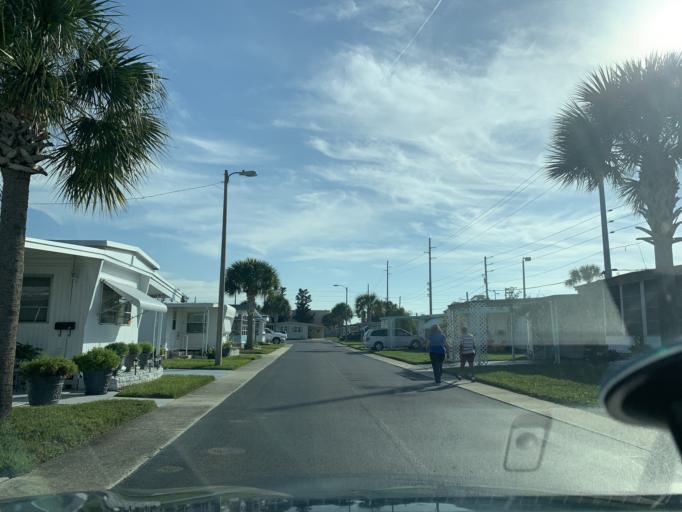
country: US
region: Florida
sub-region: Pinellas County
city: Largo
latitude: 27.8964
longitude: -82.7828
